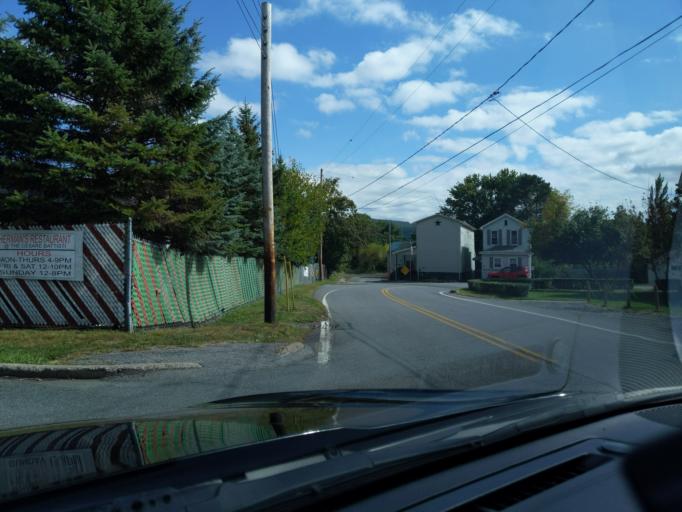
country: US
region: Pennsylvania
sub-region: Blair County
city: Lakemont
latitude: 40.4870
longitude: -78.4206
